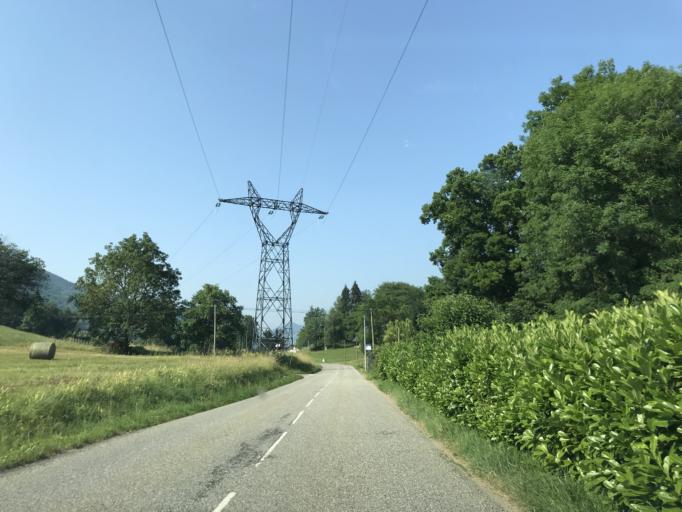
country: FR
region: Rhone-Alpes
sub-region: Departement de la Savoie
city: La Rochette
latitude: 45.4298
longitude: 6.1006
